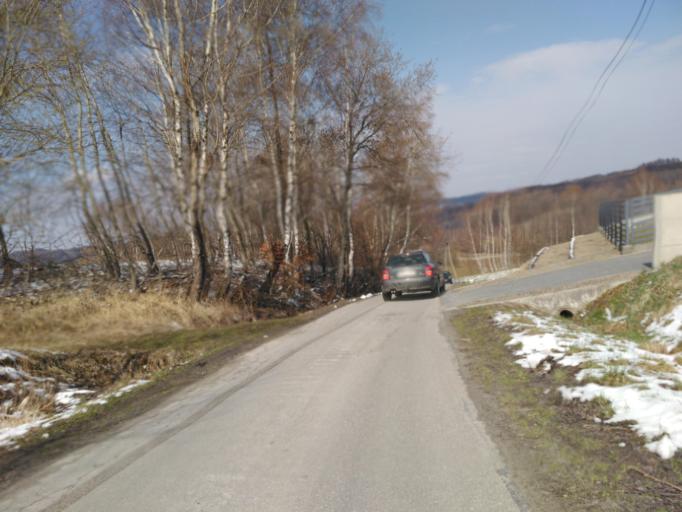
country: PL
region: Subcarpathian Voivodeship
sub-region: Powiat ropczycko-sedziszowski
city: Niedzwiada
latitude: 49.9985
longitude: 21.5698
